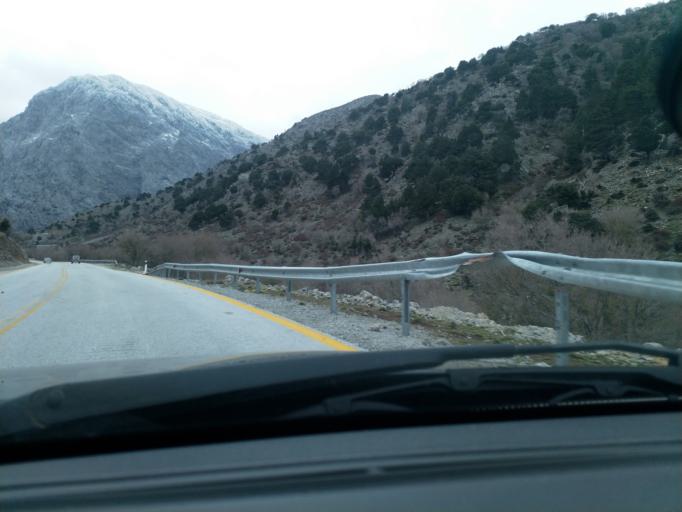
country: GR
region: Crete
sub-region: Nomos Chanias
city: Perivolia
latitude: 35.3143
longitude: 23.9155
